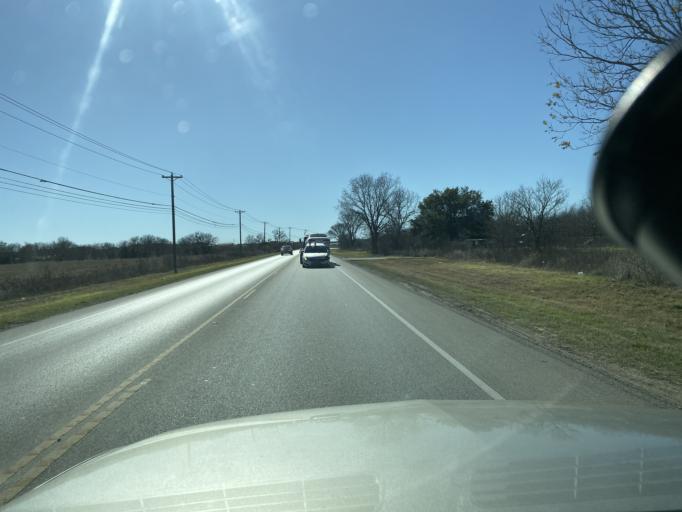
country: US
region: Texas
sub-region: Travis County
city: Garfield
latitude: 30.1752
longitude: -97.6500
